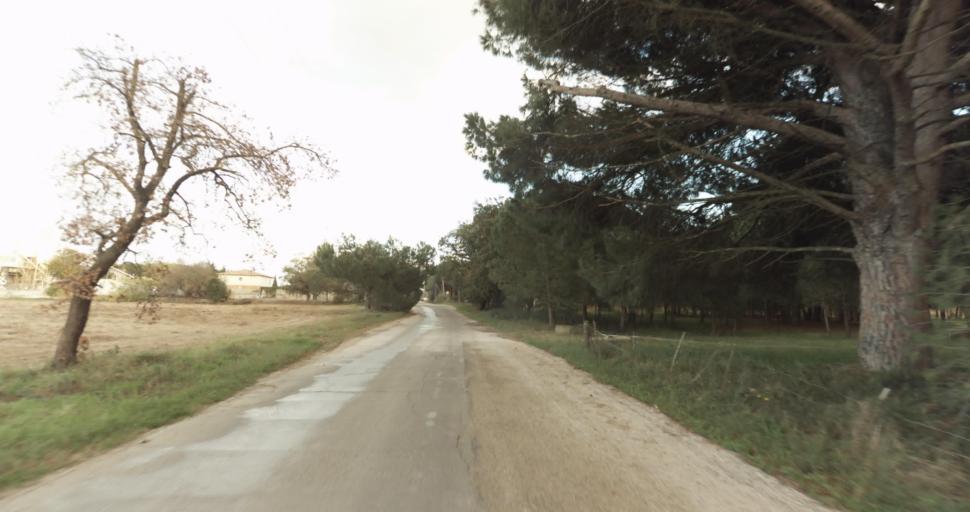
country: FR
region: Languedoc-Roussillon
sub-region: Departement du Gard
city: Aigues-Mortes
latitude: 43.5835
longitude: 4.1905
